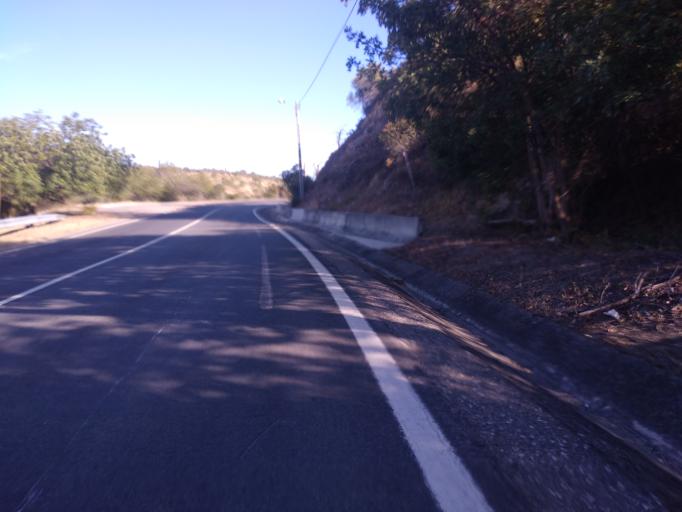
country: PT
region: Faro
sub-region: Sao Bras de Alportel
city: Sao Bras de Alportel
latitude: 37.1043
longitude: -7.9059
